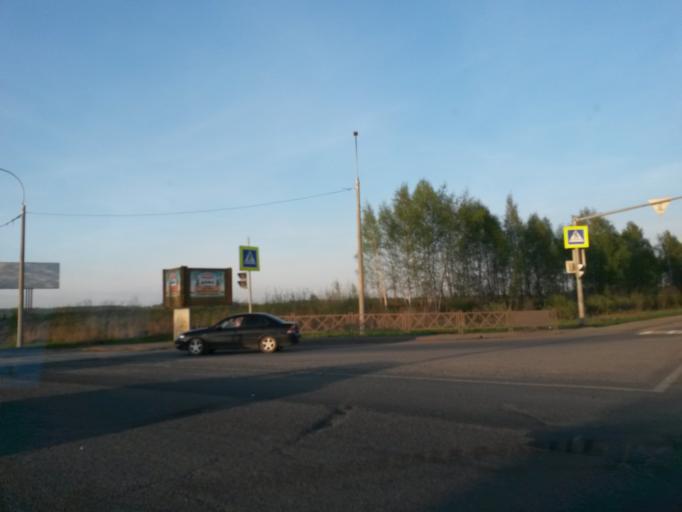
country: RU
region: Jaroslavl
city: Yaroslavl
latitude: 57.6477
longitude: 39.7475
